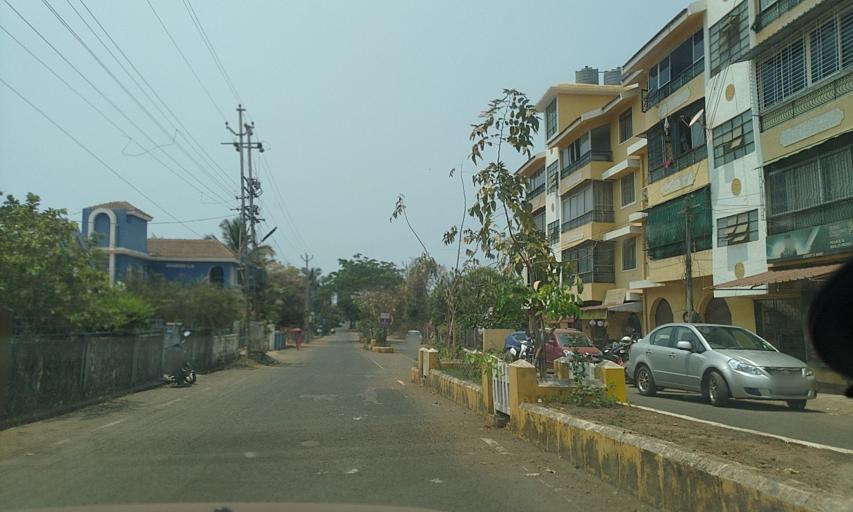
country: IN
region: Goa
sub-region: North Goa
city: Panaji
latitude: 15.5245
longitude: 73.8238
